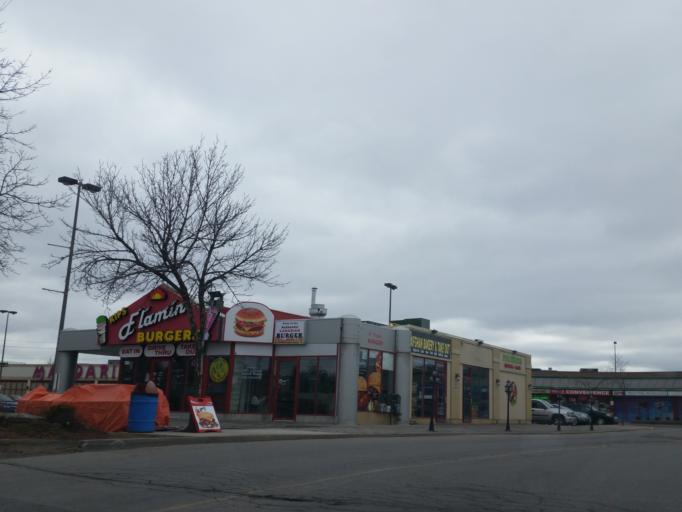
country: CA
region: Ontario
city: Ajax
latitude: 43.8490
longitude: -79.0721
